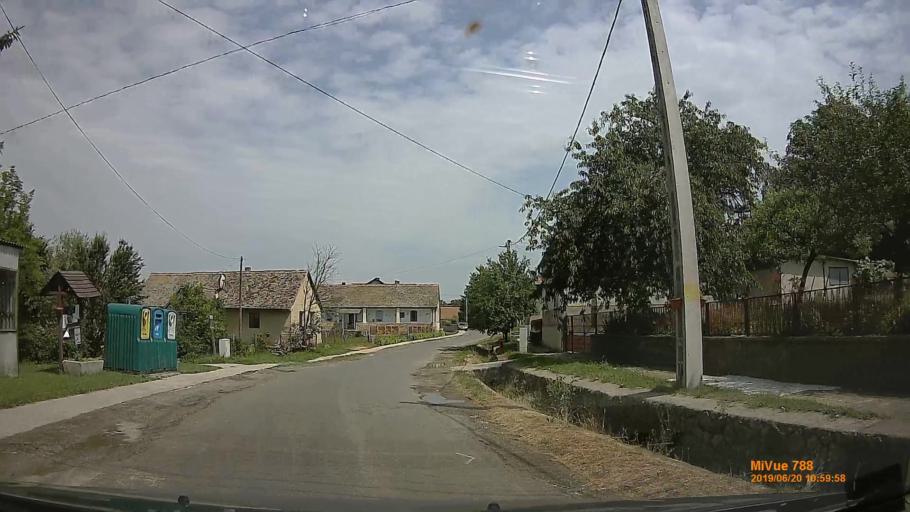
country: HU
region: Baranya
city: Mecseknadasd
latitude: 46.1701
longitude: 18.5131
